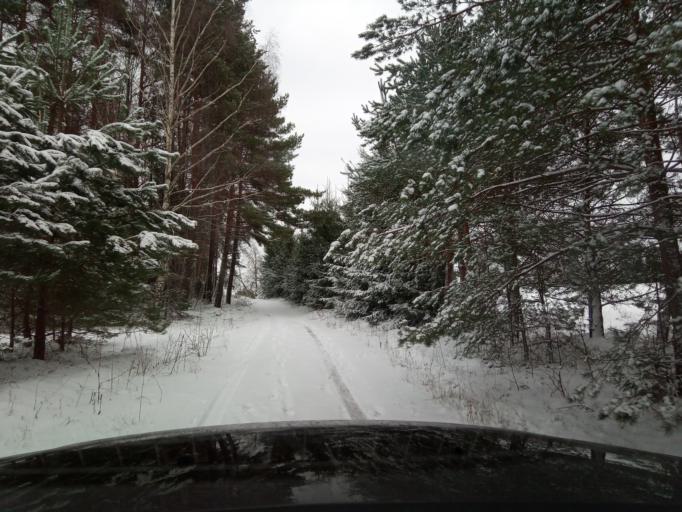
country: LT
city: Zarasai
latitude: 55.6756
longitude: 26.0281
